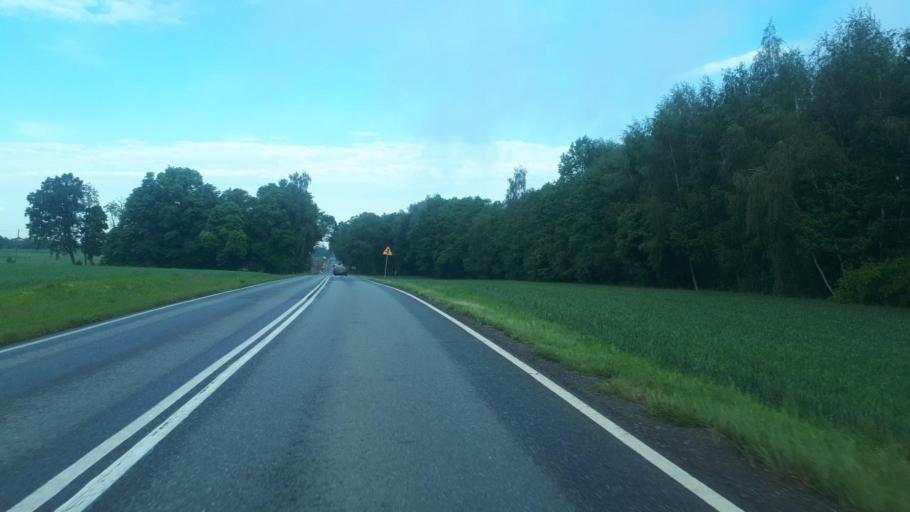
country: PL
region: Silesian Voivodeship
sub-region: Powiat pszczynski
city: Miedzna
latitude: 49.9702
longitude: 19.0301
